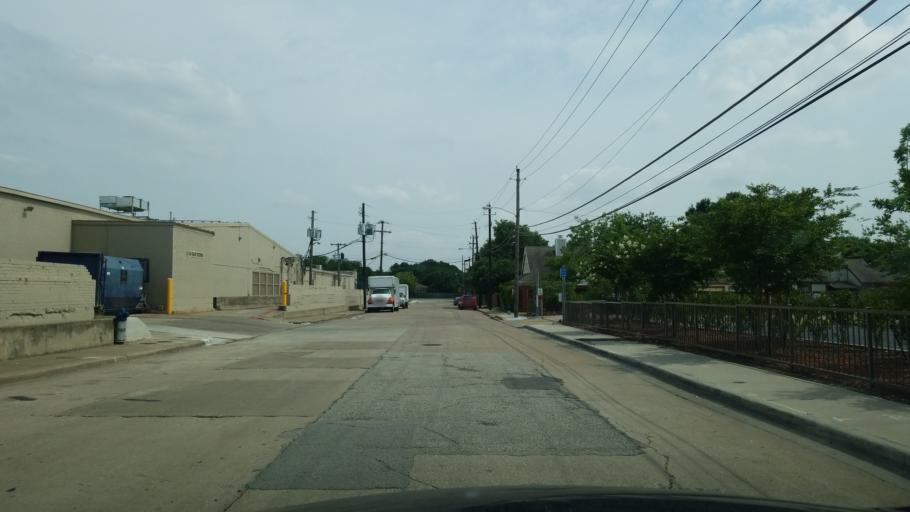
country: US
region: Texas
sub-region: Dallas County
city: Farmers Branch
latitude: 32.8970
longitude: -96.8721
